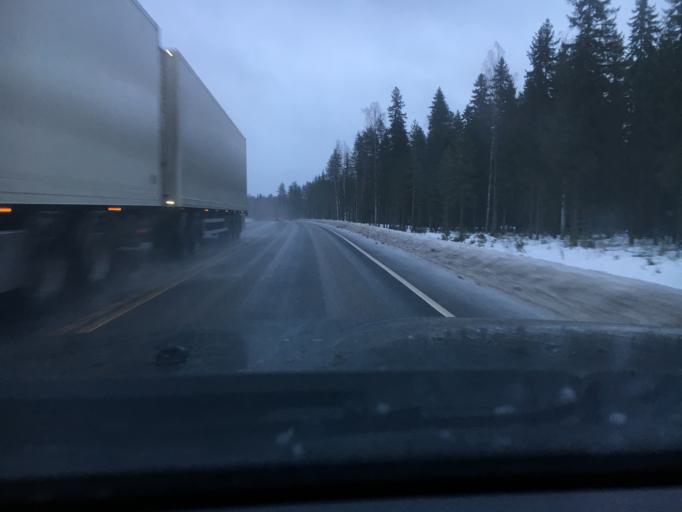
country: FI
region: Central Finland
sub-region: Jyvaeskylae
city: Hankasalmi
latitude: 62.3912
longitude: 26.6303
